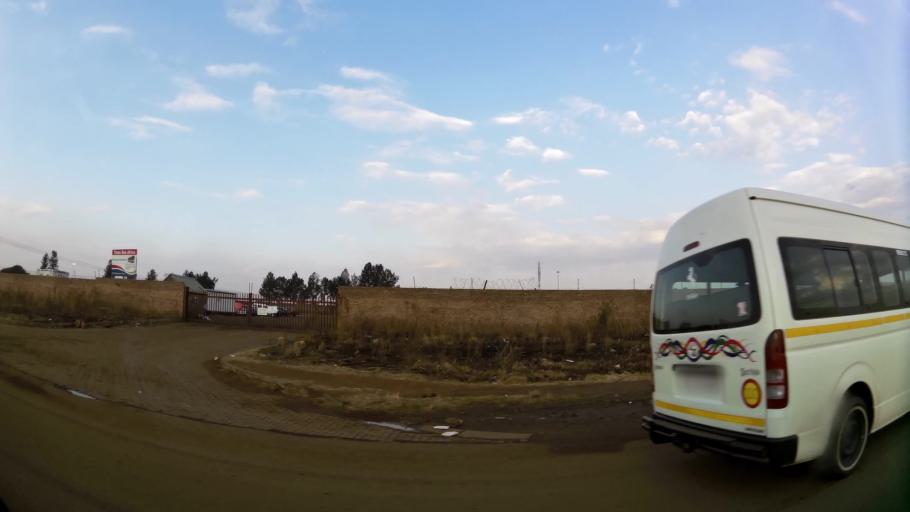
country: ZA
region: Gauteng
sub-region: City of Johannesburg Metropolitan Municipality
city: Orange Farm
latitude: -26.5550
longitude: 27.8304
